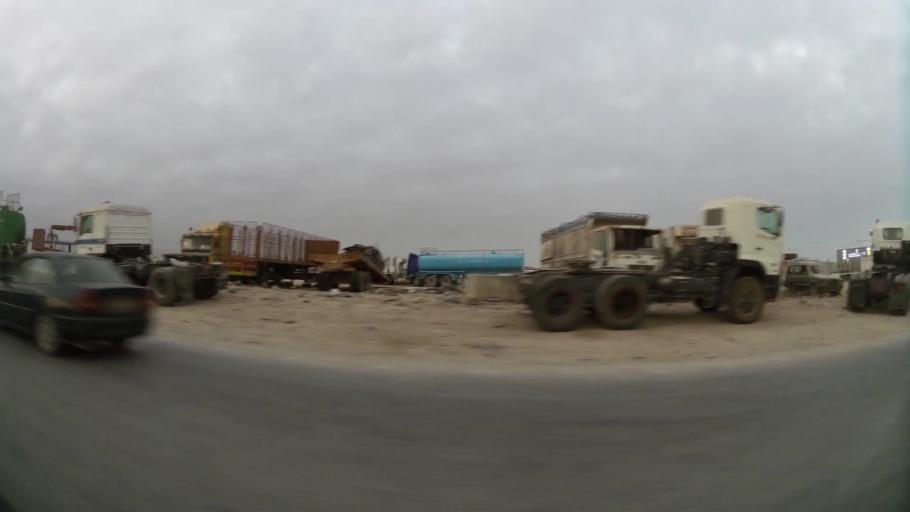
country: OM
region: Zufar
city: Salalah
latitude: 17.0258
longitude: 54.0424
